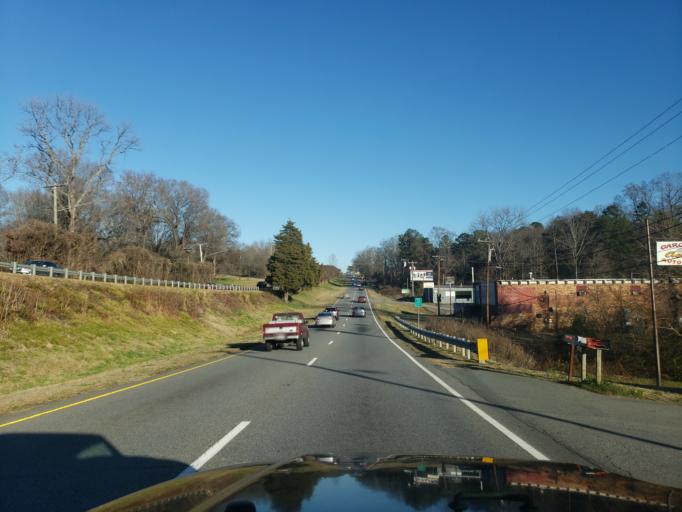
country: US
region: North Carolina
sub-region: Gaston County
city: South Gastonia
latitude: 35.2574
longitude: -81.2359
